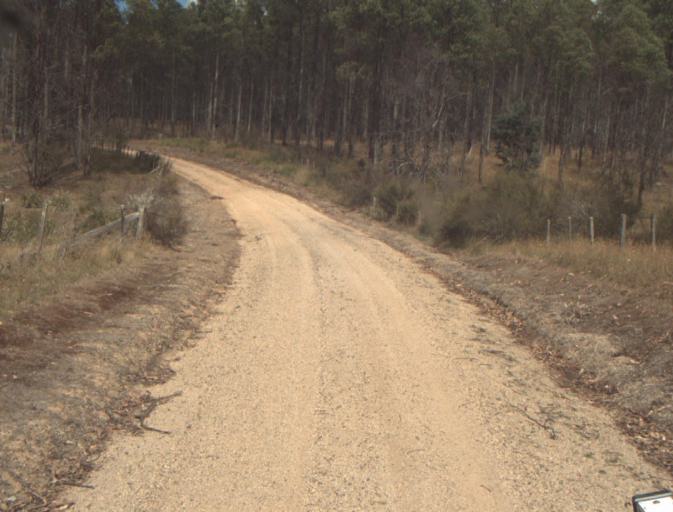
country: AU
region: Tasmania
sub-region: Dorset
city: Scottsdale
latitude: -41.4112
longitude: 147.5267
